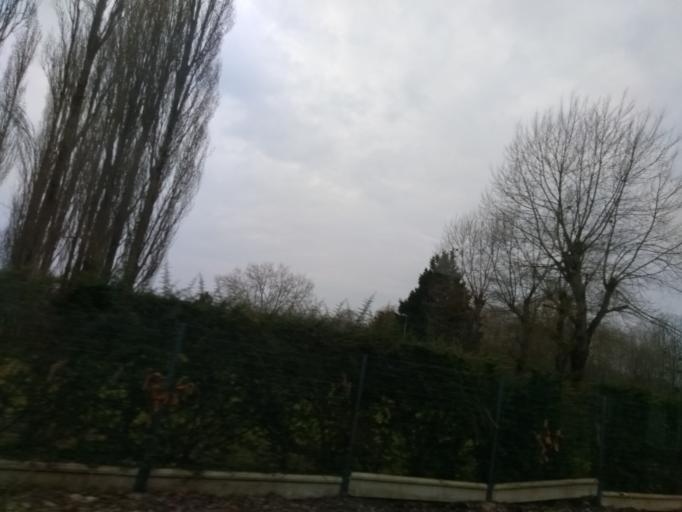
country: FR
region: Picardie
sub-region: Departement de l'Oise
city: Jaux
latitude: 49.3925
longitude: 2.7839
